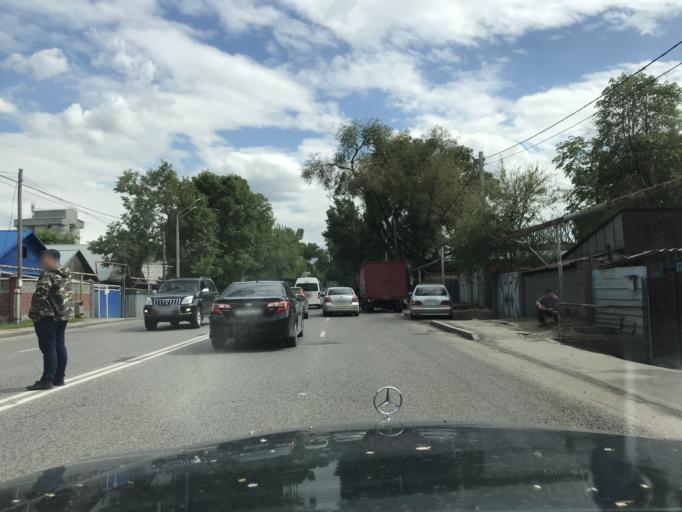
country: KZ
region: Almaty Qalasy
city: Almaty
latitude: 43.2902
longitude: 76.9011
